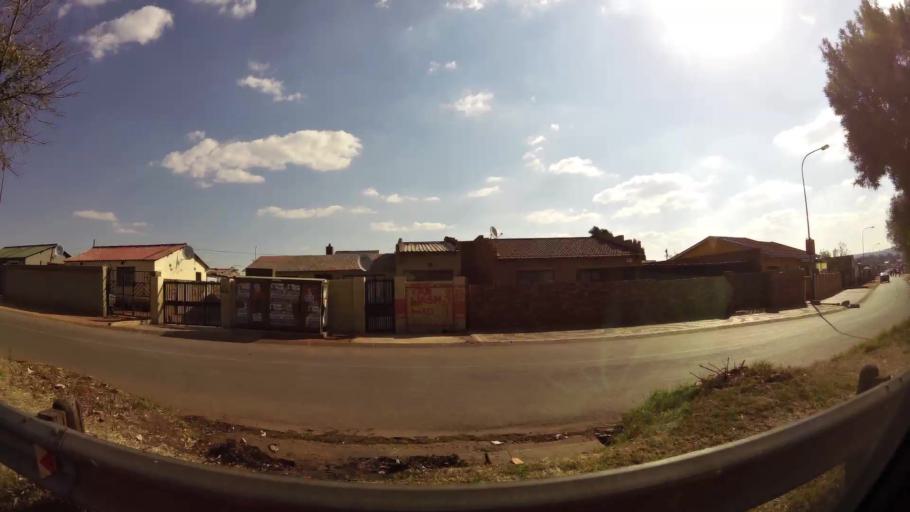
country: ZA
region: Gauteng
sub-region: City of Johannesburg Metropolitan Municipality
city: Soweto
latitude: -26.2266
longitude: 27.8728
